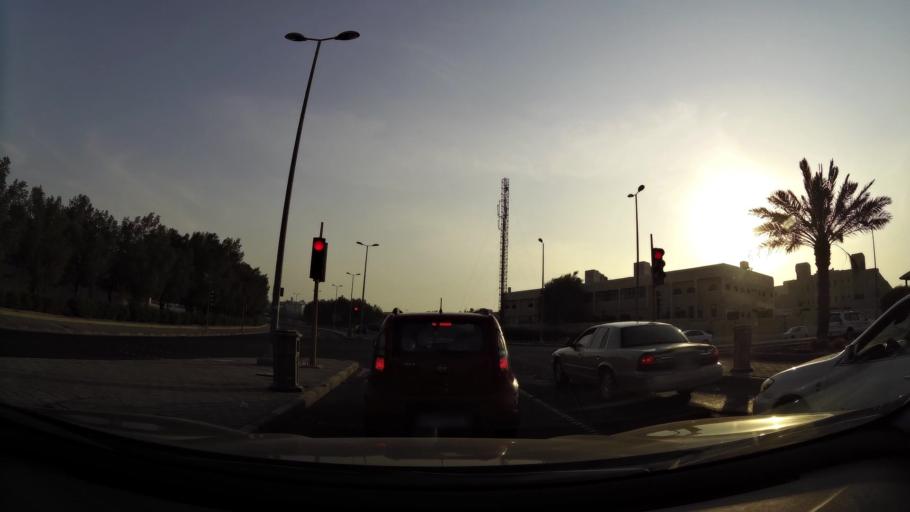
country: KW
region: Mubarak al Kabir
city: Sabah as Salim
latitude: 29.2438
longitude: 48.0612
